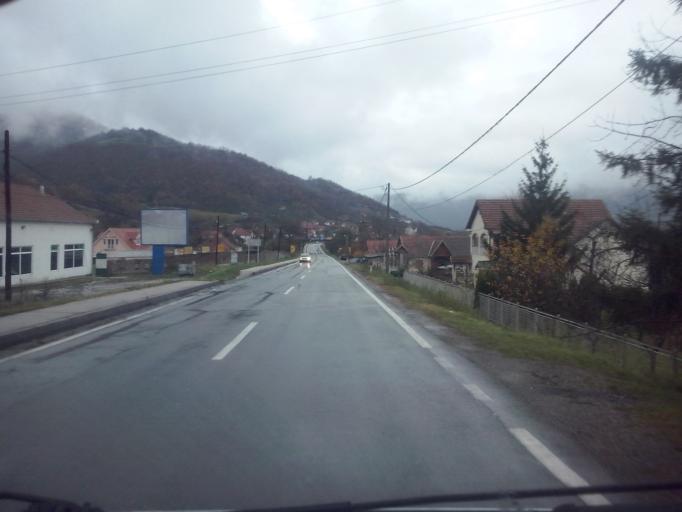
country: RS
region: Central Serbia
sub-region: Raski Okrug
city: Raska
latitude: 43.3938
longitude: 20.6389
